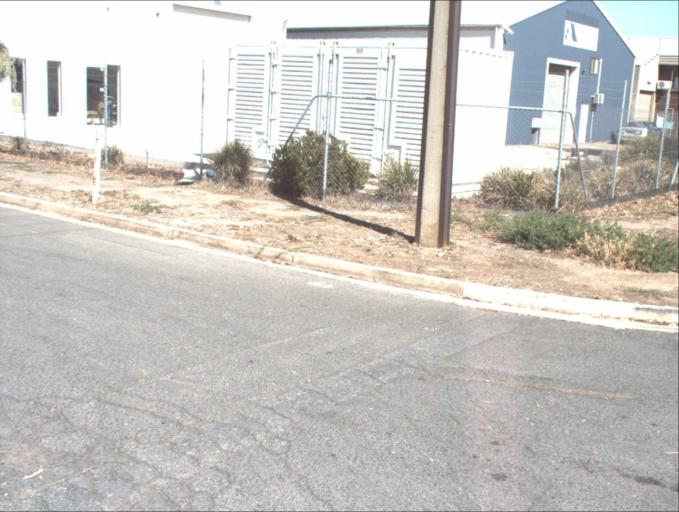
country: AU
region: South Australia
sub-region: Charles Sturt
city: Woodville North
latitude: -34.8352
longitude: 138.5591
